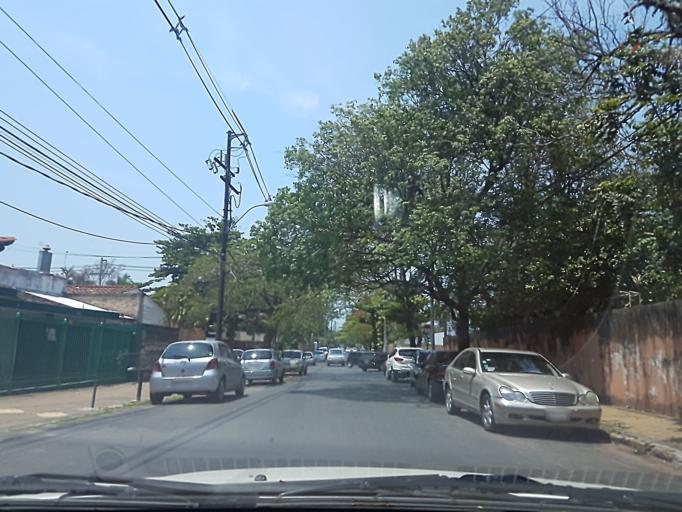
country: PY
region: Asuncion
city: Asuncion
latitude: -25.2894
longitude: -57.6067
